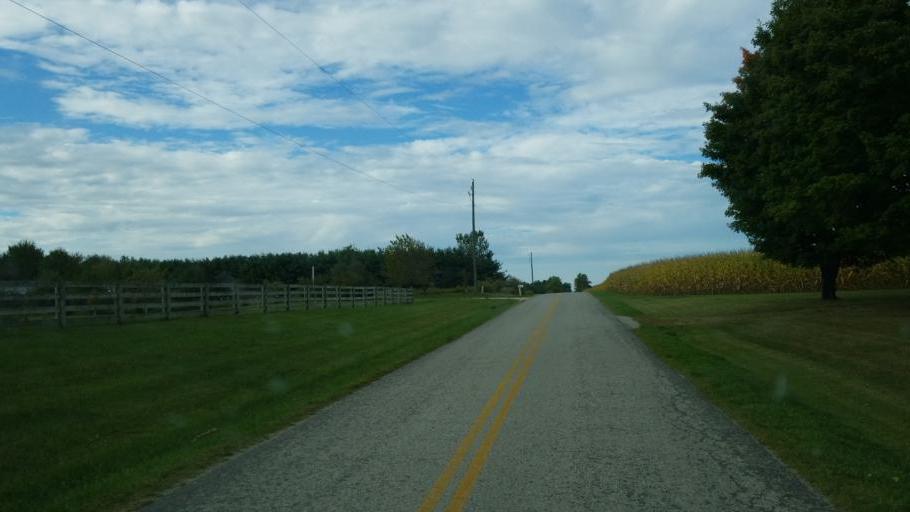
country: US
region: Ohio
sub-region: Knox County
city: Centerburg
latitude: 40.2887
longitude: -82.7737
